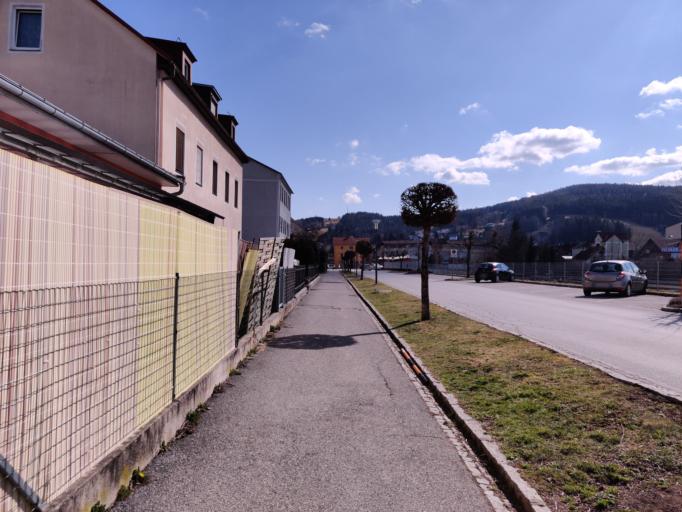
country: AT
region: Styria
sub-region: Politischer Bezirk Voitsberg
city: Voitsberg
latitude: 47.0452
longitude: 15.1487
